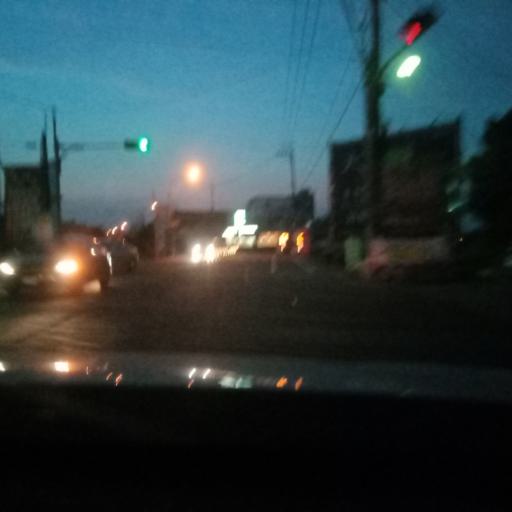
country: TW
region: Taiwan
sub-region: Hsinchu
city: Zhubei
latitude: 24.8994
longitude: 121.0564
